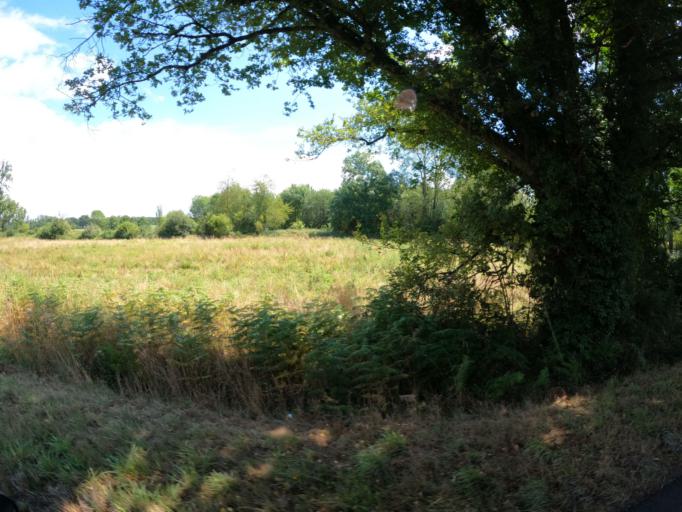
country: FR
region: Pays de la Loire
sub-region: Departement de Maine-et-Loire
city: Champigne
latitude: 47.6385
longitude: -0.5790
